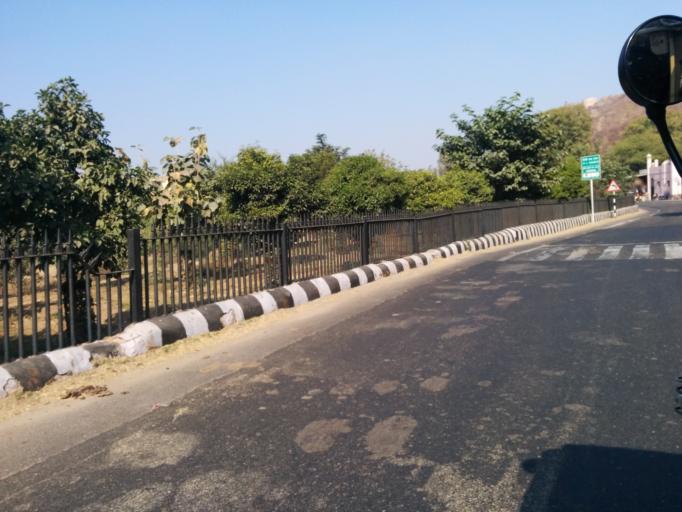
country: IN
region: Rajasthan
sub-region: Jaipur
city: Jaipur
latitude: 26.9762
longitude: 75.8513
